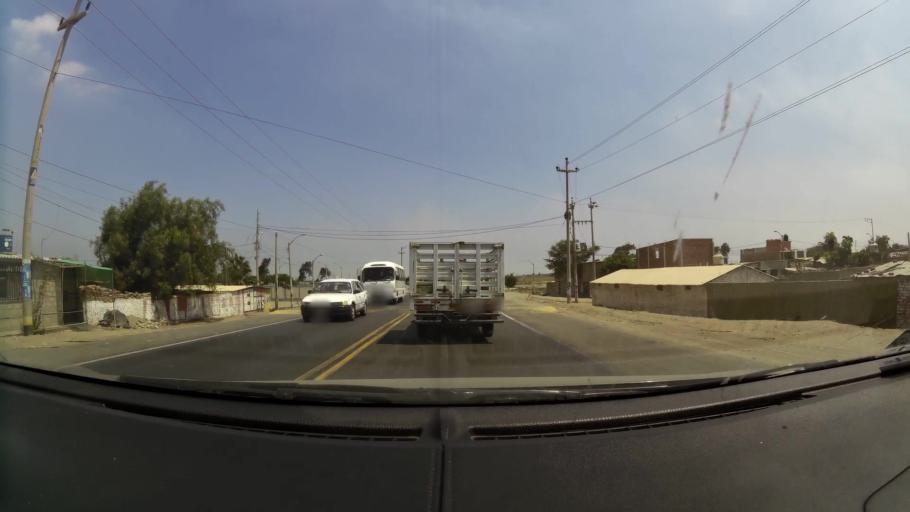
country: PE
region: La Libertad
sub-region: Provincia de Pacasmayo
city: San Pedro de Lloc
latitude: -7.4182
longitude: -79.5254
